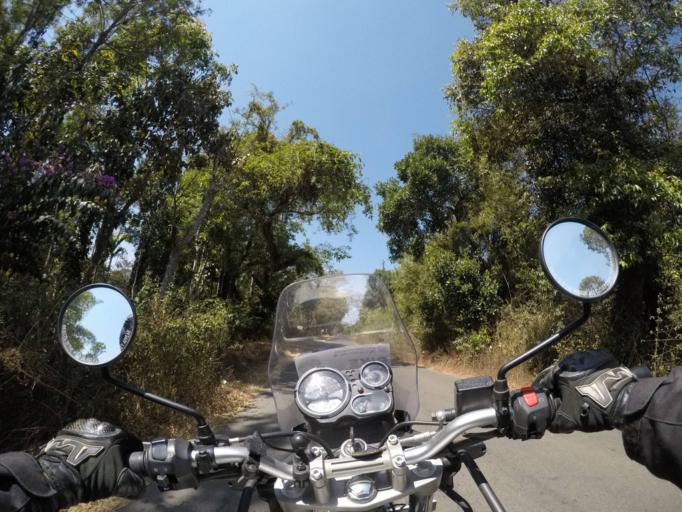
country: IN
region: Karnataka
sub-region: Chikmagalur
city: Mudigere
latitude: 13.0747
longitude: 75.6832
